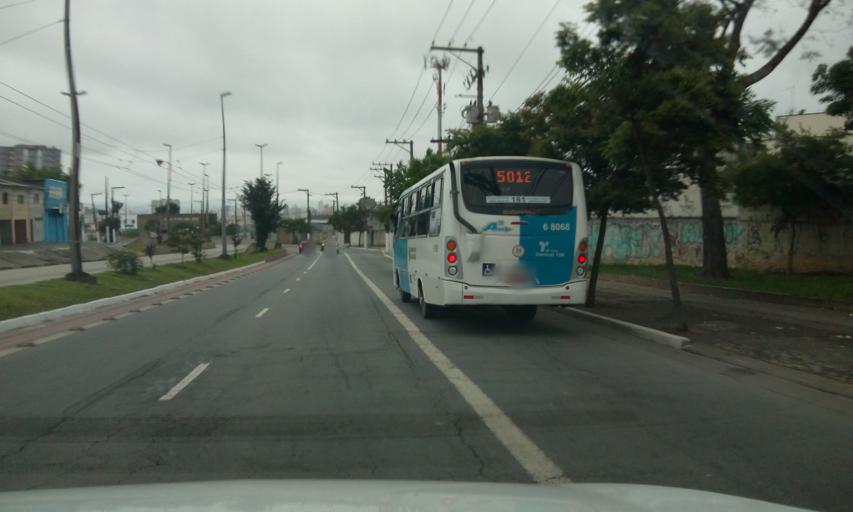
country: BR
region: Sao Paulo
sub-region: Diadema
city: Diadema
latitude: -23.6593
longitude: -46.6362
